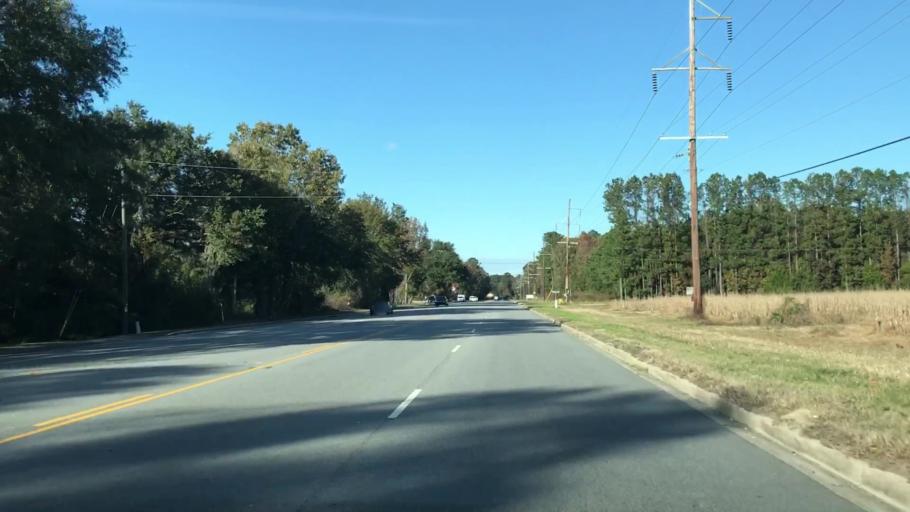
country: US
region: South Carolina
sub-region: Beaufort County
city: Laurel Bay
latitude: 32.5760
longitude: -80.7432
